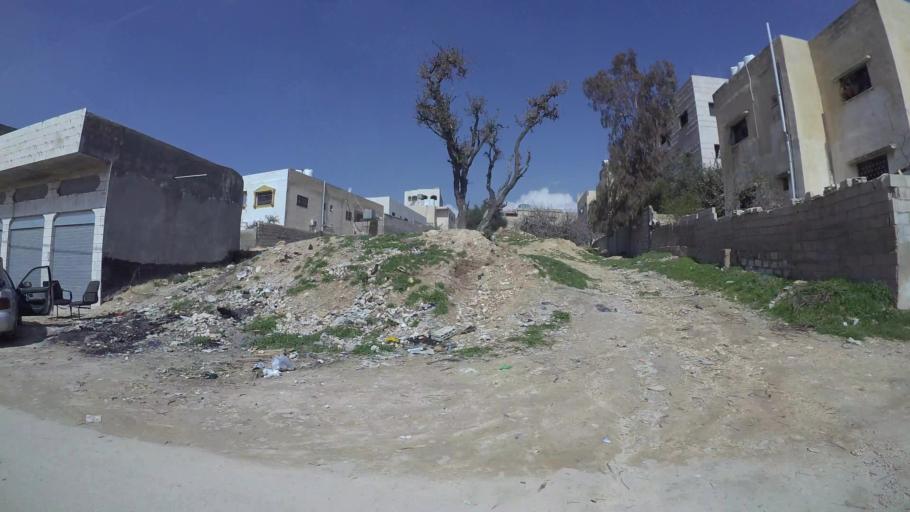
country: JO
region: Amman
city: Al Bunayyat ash Shamaliyah
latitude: 31.9000
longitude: 35.9028
